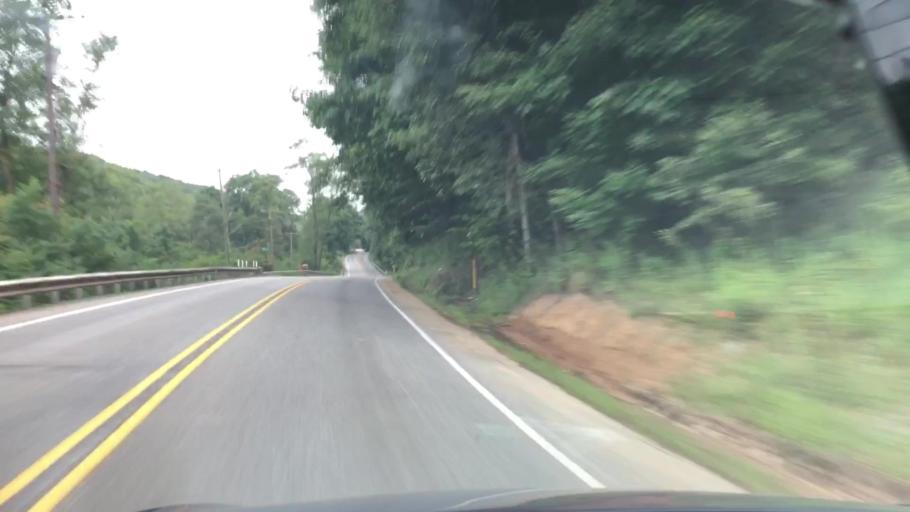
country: US
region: Pennsylvania
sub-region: Venango County
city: Hasson Heights
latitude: 41.5018
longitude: -79.7018
